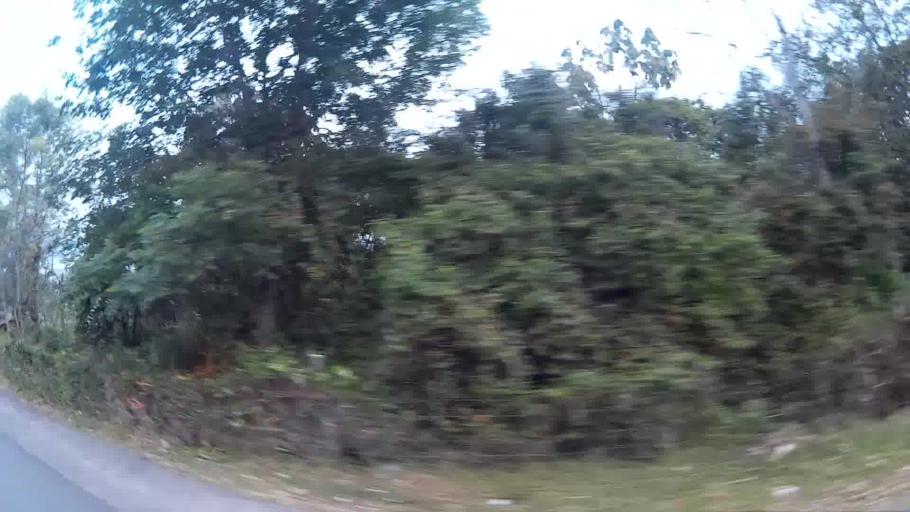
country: CO
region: Quindio
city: Filandia
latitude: 4.7230
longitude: -75.6254
